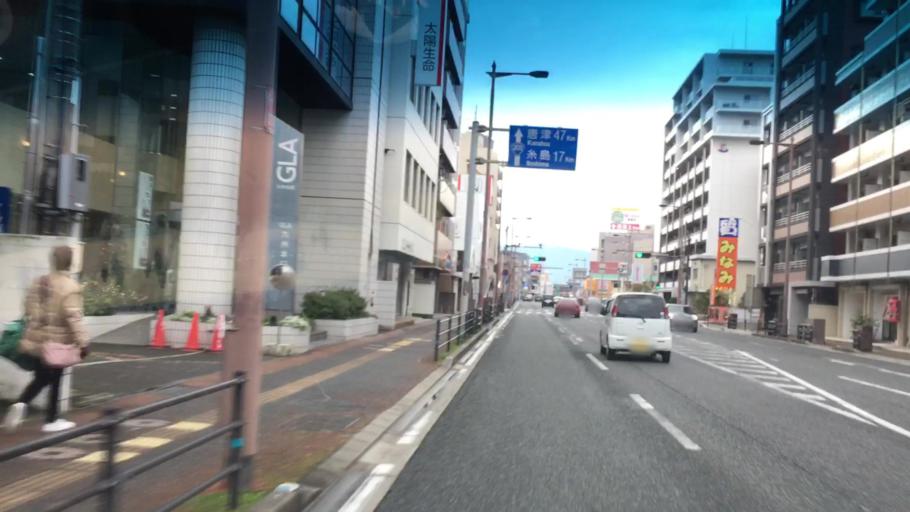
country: JP
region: Fukuoka
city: Fukuoka-shi
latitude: 33.5695
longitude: 130.3544
